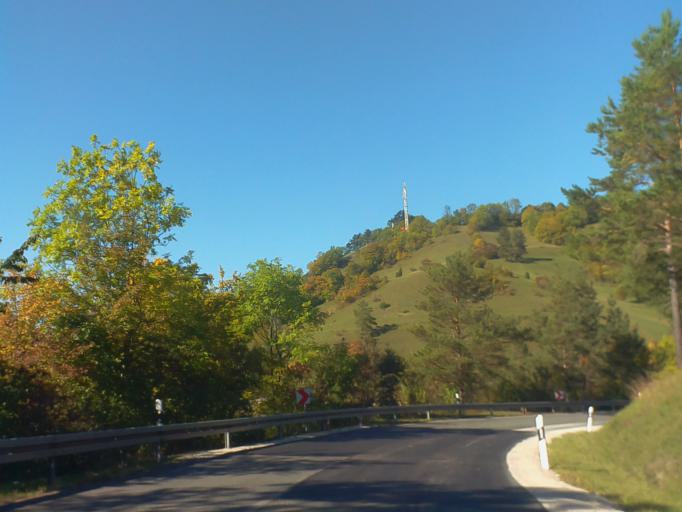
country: DE
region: Thuringia
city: Seitenroda
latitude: 50.8012
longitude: 11.6059
